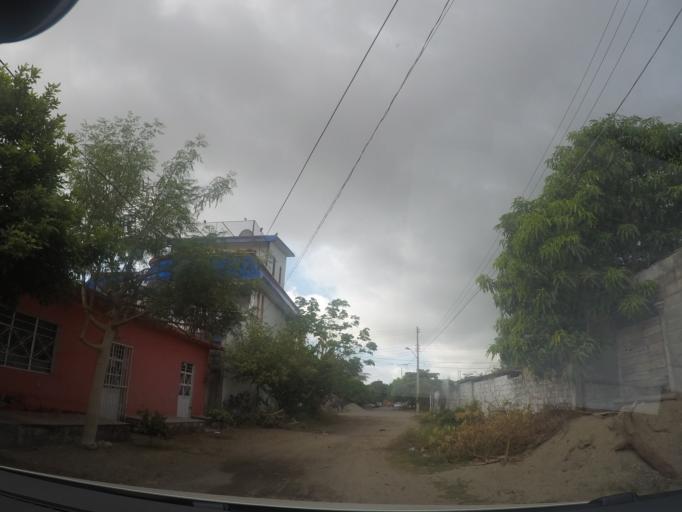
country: MX
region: Oaxaca
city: Juchitan de Zaragoza
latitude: 16.4327
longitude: -95.0325
